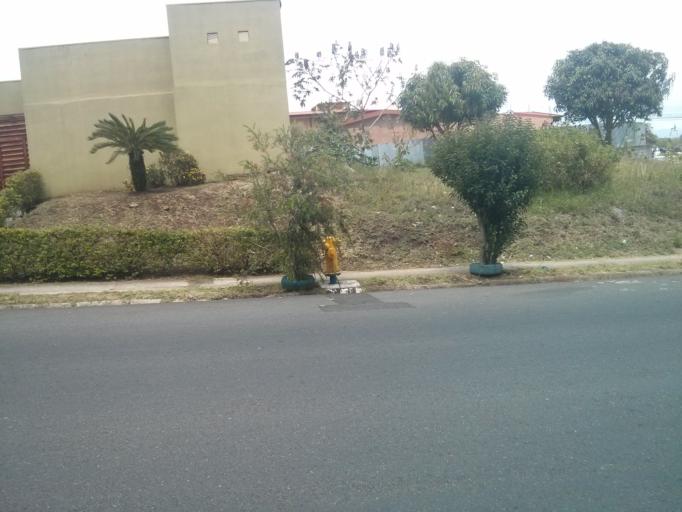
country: CR
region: Heredia
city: Angeles
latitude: 10.0113
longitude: -84.0542
